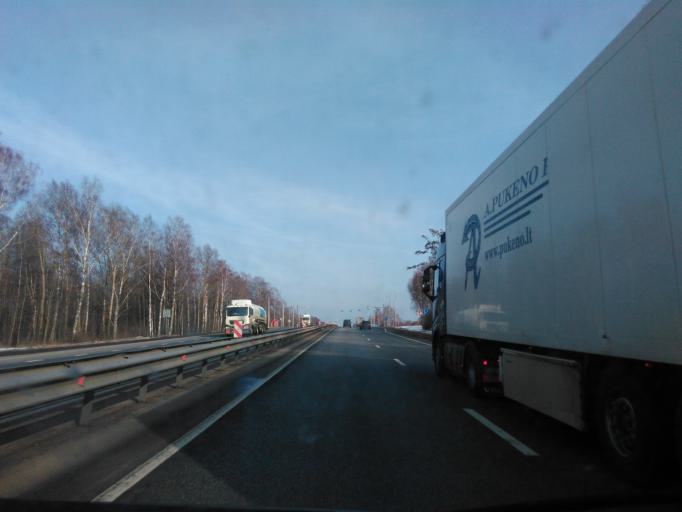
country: RU
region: Smolensk
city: Kholm-Zhirkovskiy
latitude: 55.1884
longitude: 33.7492
